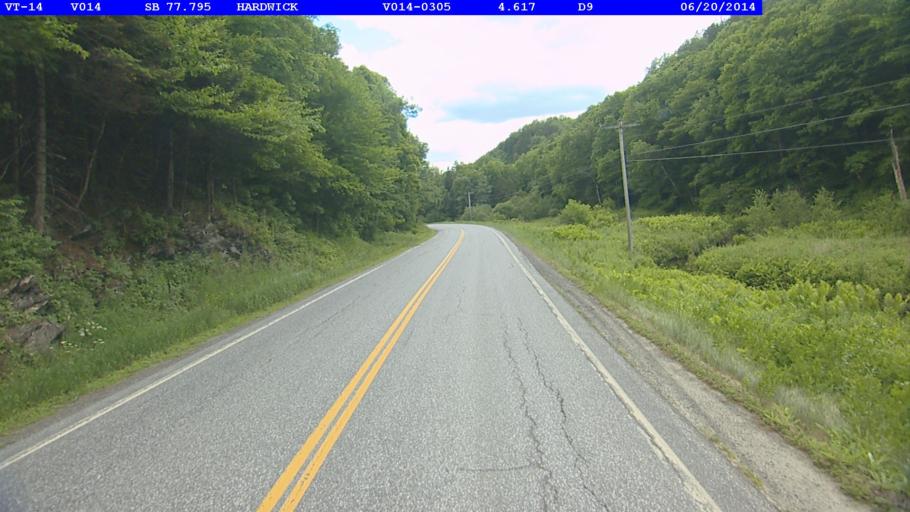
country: US
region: Vermont
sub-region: Caledonia County
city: Hardwick
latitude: 44.5600
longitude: -72.3682
